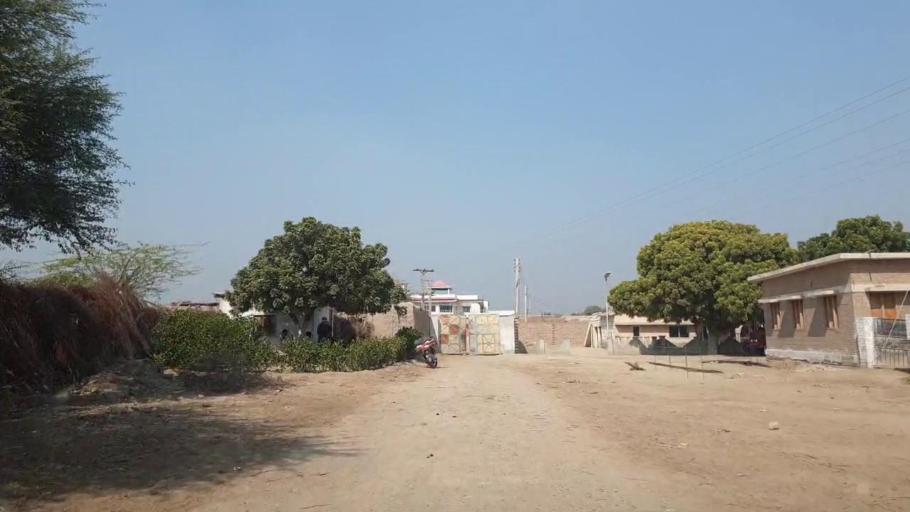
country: PK
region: Sindh
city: Tando Allahyar
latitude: 25.5054
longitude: 68.8352
